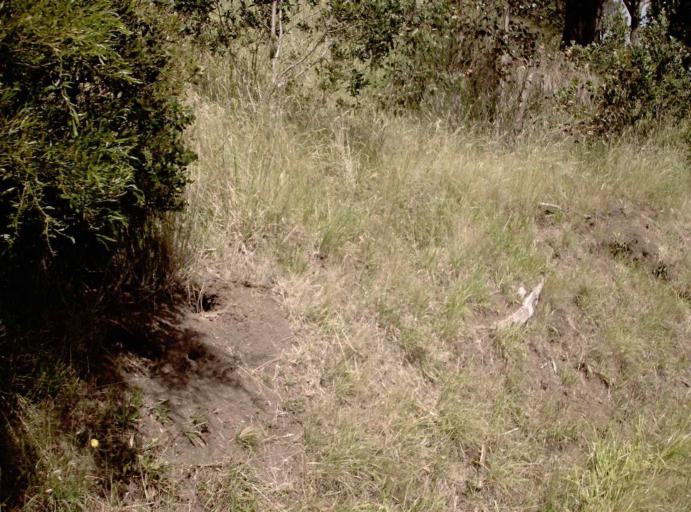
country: AU
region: Victoria
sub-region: Latrobe
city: Traralgon
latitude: -38.3229
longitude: 146.5699
